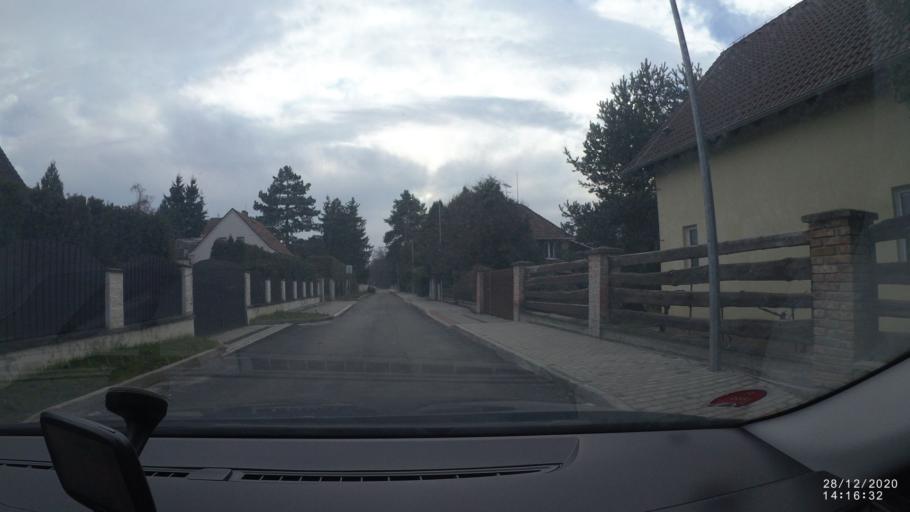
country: CZ
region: Central Bohemia
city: Sestajovice
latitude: 50.0990
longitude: 14.6668
